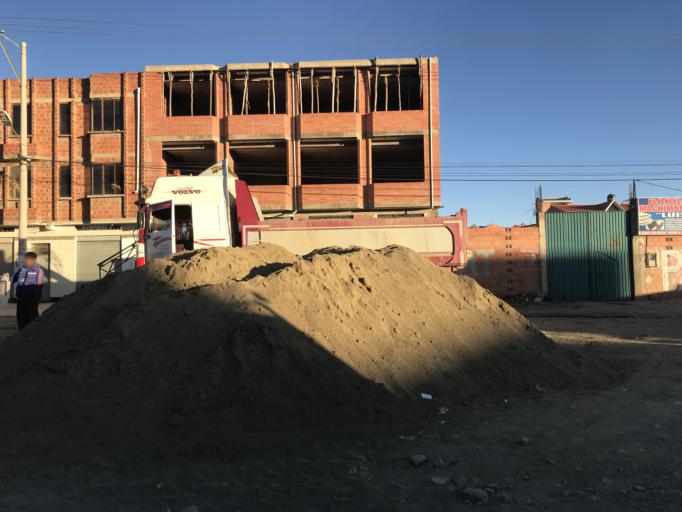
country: BO
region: La Paz
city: La Paz
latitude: -16.5044
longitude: -68.2498
